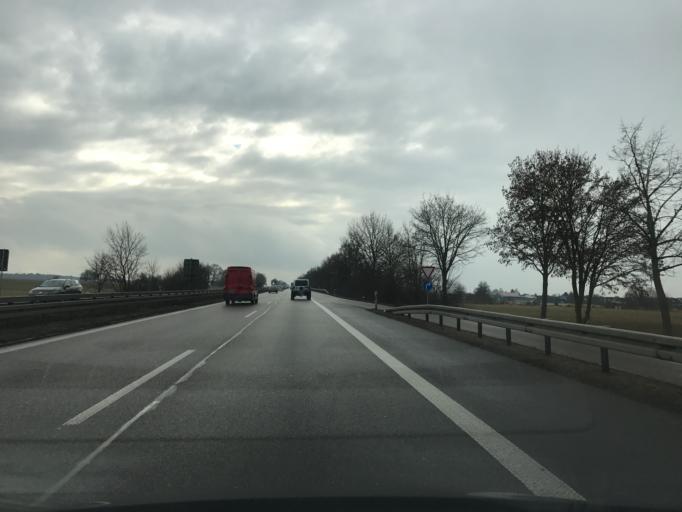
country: DE
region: Baden-Wuerttemberg
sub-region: Tuebingen Region
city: Staig
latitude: 48.3435
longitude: 9.9509
